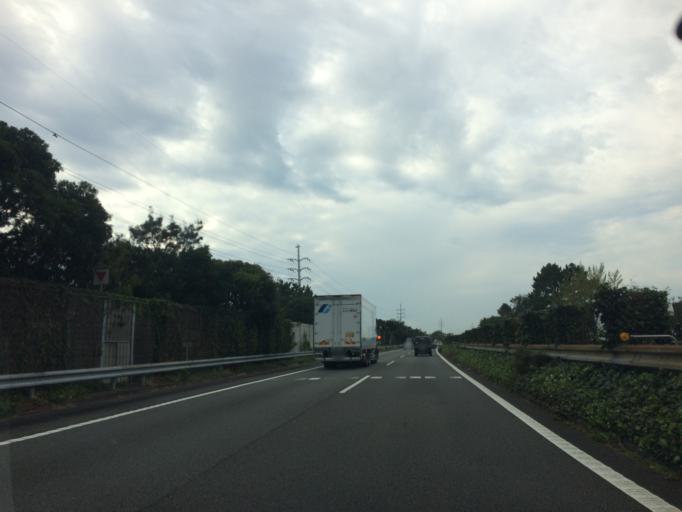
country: JP
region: Shizuoka
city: Fujieda
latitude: 34.8444
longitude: 138.2822
